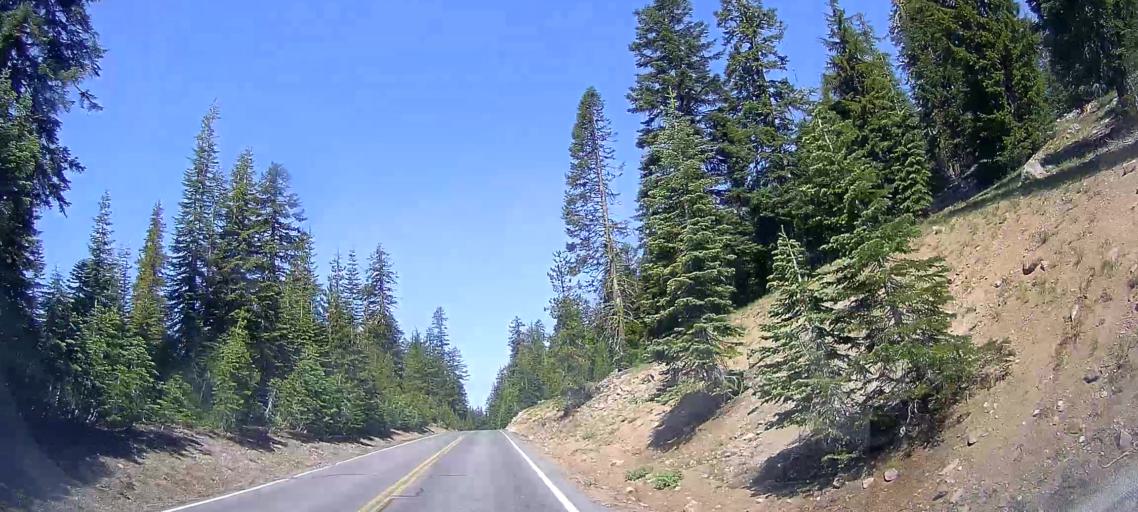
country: US
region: Oregon
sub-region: Klamath County
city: Klamath Falls
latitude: 42.8798
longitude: -122.1146
